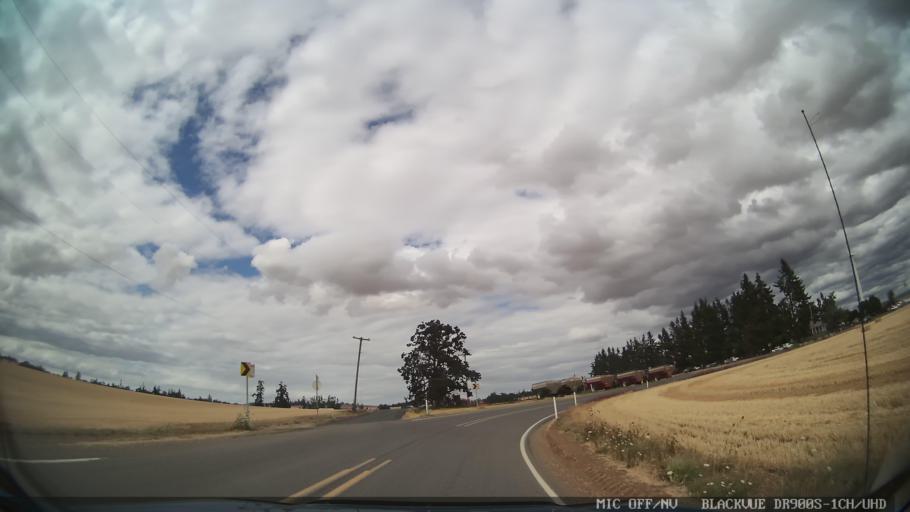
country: US
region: Oregon
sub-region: Marion County
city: Sublimity
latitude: 44.8660
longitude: -122.8107
